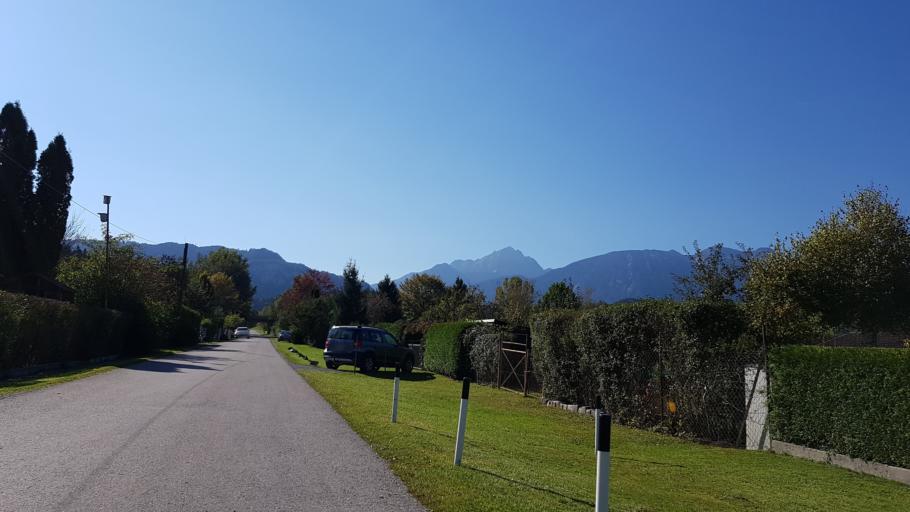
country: DE
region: Bavaria
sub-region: Swabia
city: Fuessen
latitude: 47.5825
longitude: 10.6797
